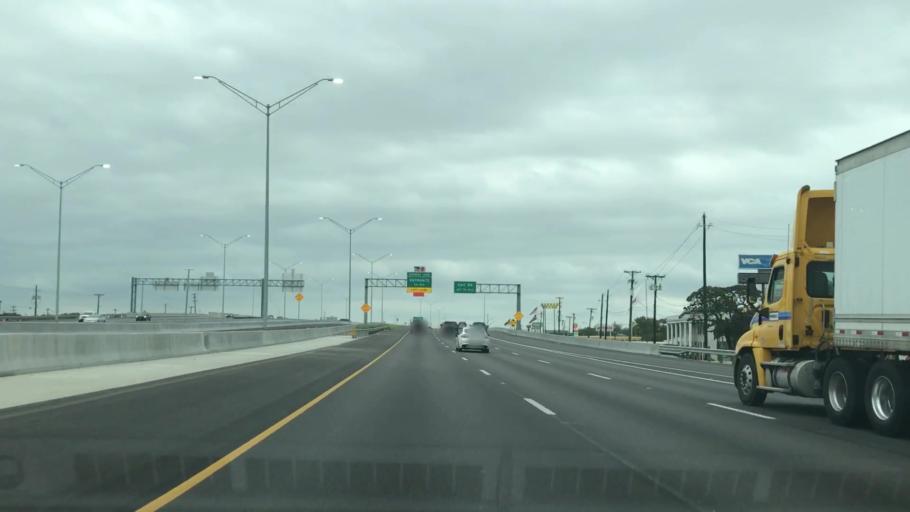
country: US
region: Texas
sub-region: Dallas County
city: Irving
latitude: 32.8367
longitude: -96.9547
